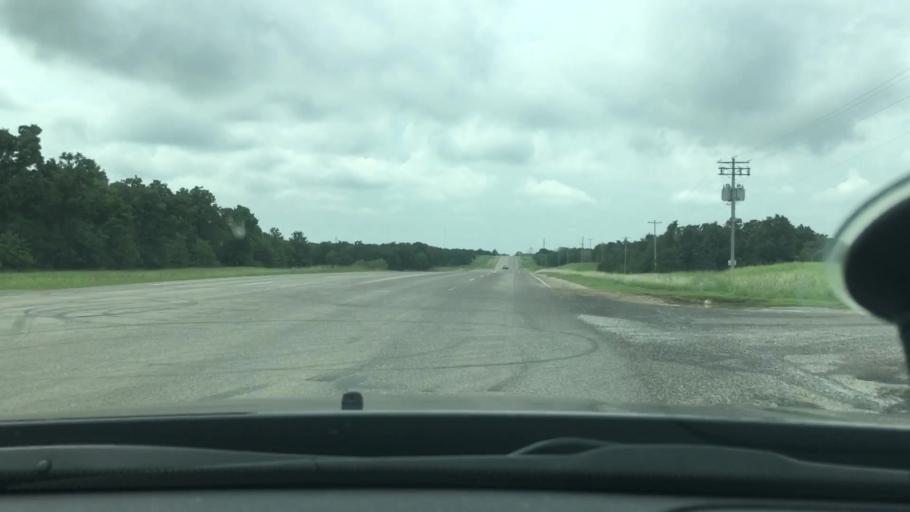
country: US
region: Oklahoma
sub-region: Carter County
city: Healdton
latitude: 34.1876
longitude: -97.4749
